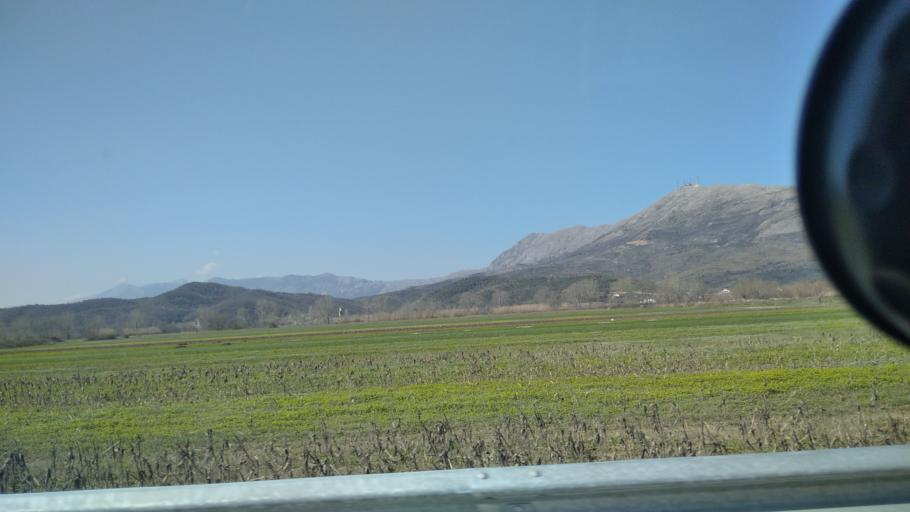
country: AL
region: Shkoder
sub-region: Rrethi i Shkodres
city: Berdica e Madhe
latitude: 42.0183
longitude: 19.4767
